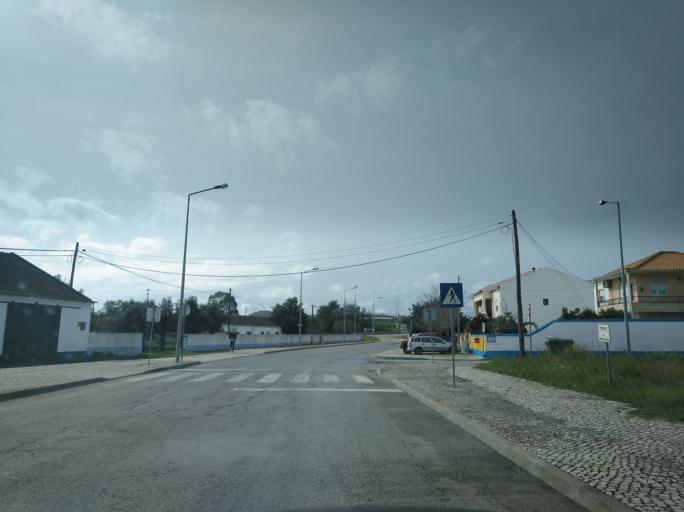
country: PT
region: Setubal
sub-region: Grandola
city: Grandola
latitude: 38.1768
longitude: -8.5732
